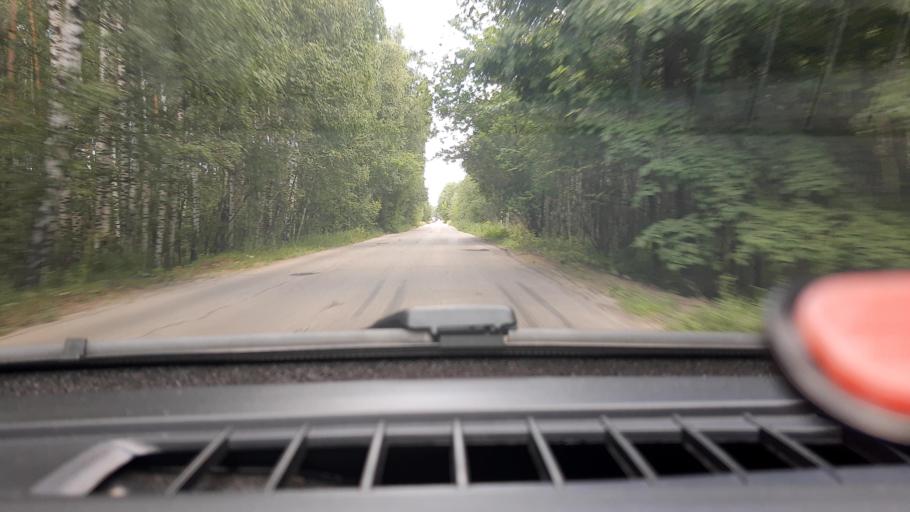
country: RU
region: Nizjnij Novgorod
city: Babino
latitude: 56.3172
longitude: 43.6244
